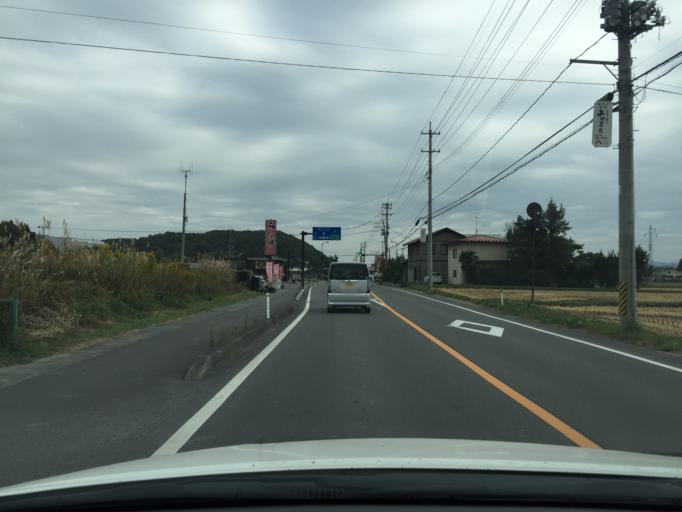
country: JP
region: Tochigi
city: Kuroiso
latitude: 37.1337
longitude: 140.1688
